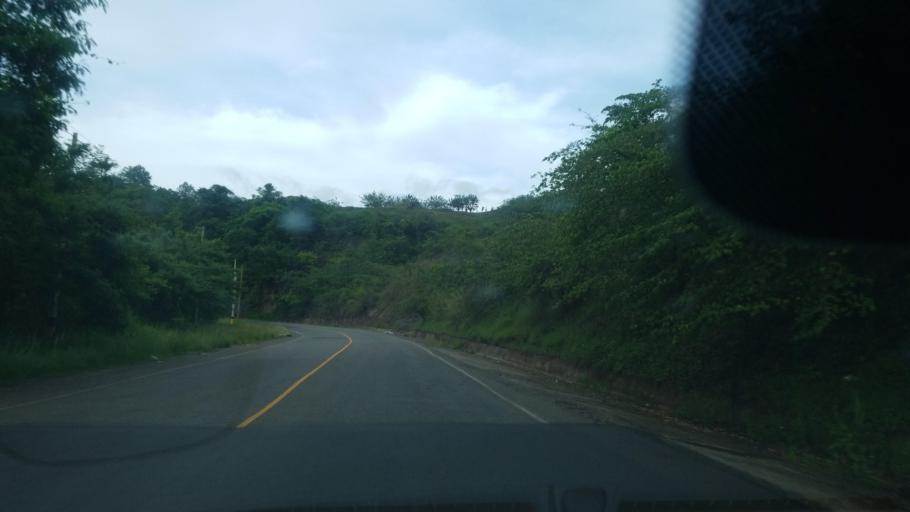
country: HN
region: Santa Barbara
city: Concepcion del Sur
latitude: 14.8132
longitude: -88.1817
